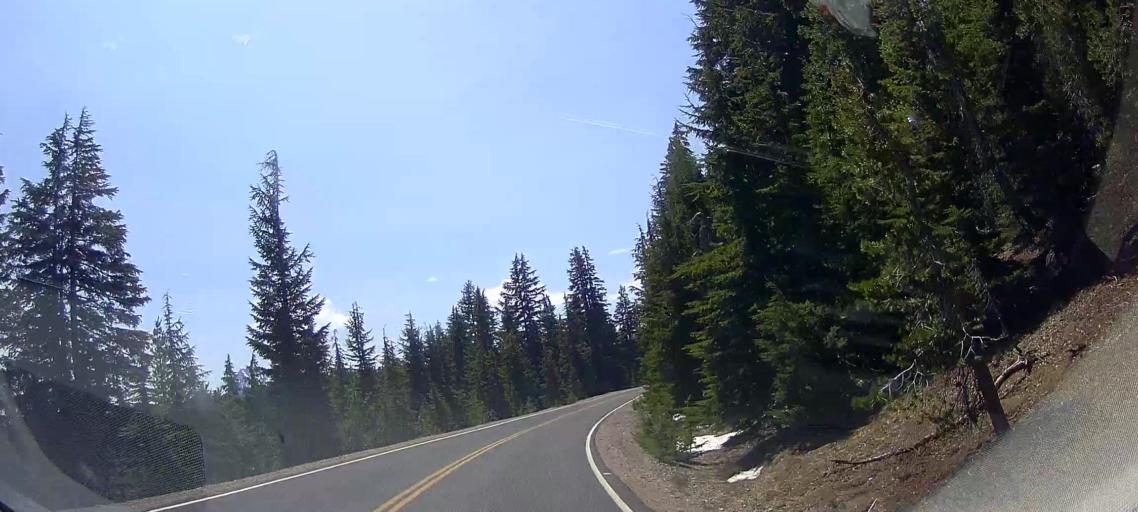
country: US
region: Oregon
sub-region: Jackson County
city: Shady Cove
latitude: 42.9806
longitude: -122.1074
